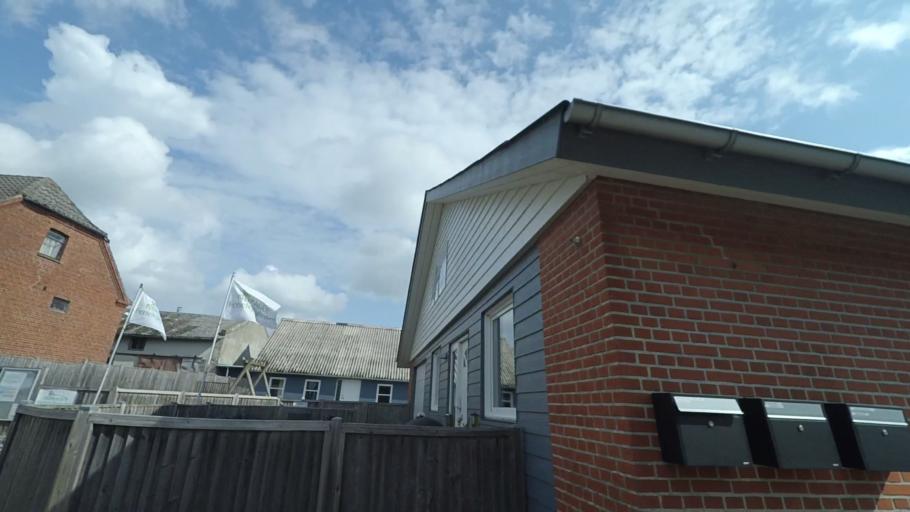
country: DK
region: Central Jutland
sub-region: Syddjurs Kommune
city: Ryomgard
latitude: 56.4773
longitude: 10.5049
